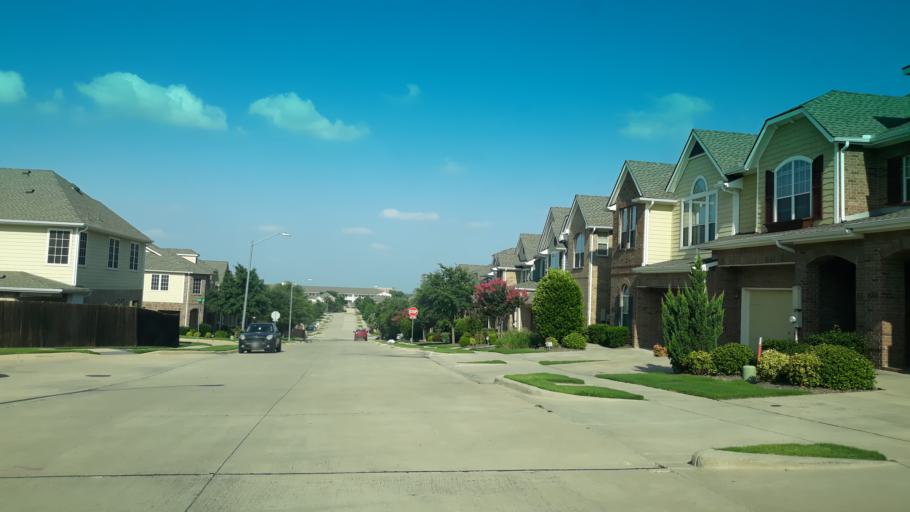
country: US
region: Texas
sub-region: Dallas County
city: Irving
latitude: 32.8646
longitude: -96.9984
